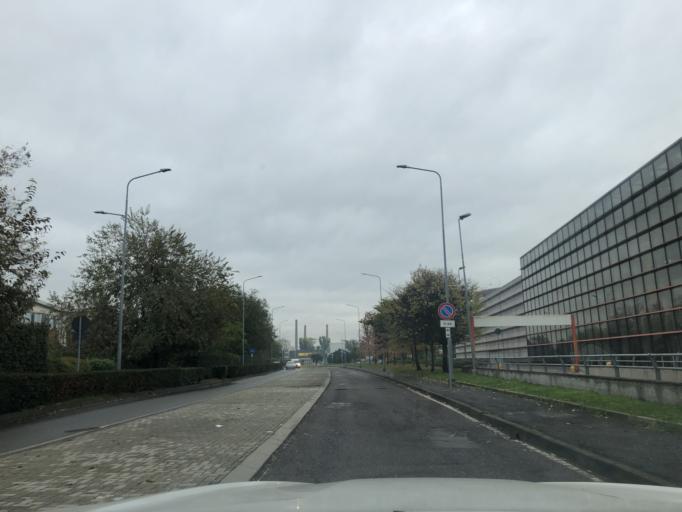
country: IT
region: Lombardy
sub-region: Citta metropolitana di Milano
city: Cesano Boscone
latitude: 45.4359
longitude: 9.0879
